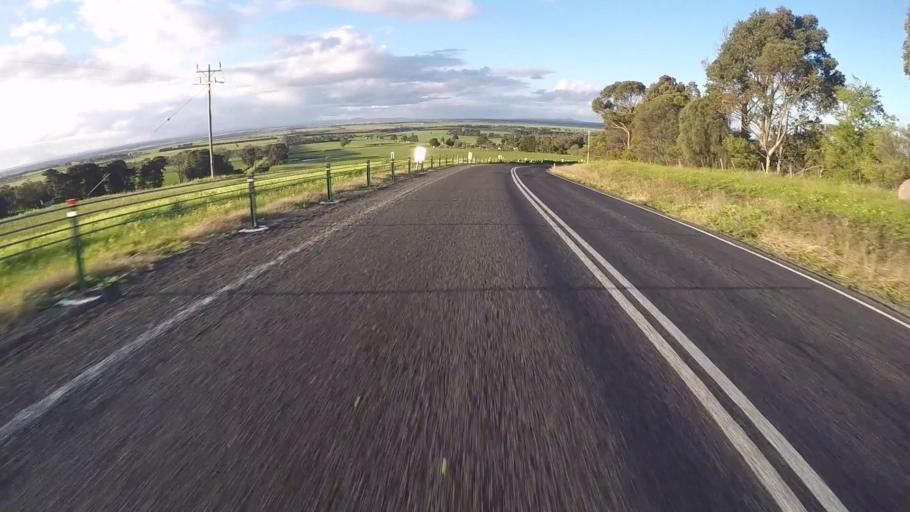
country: AU
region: Victoria
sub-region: Greater Geelong
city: Wandana Heights
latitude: -38.1559
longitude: 144.1635
